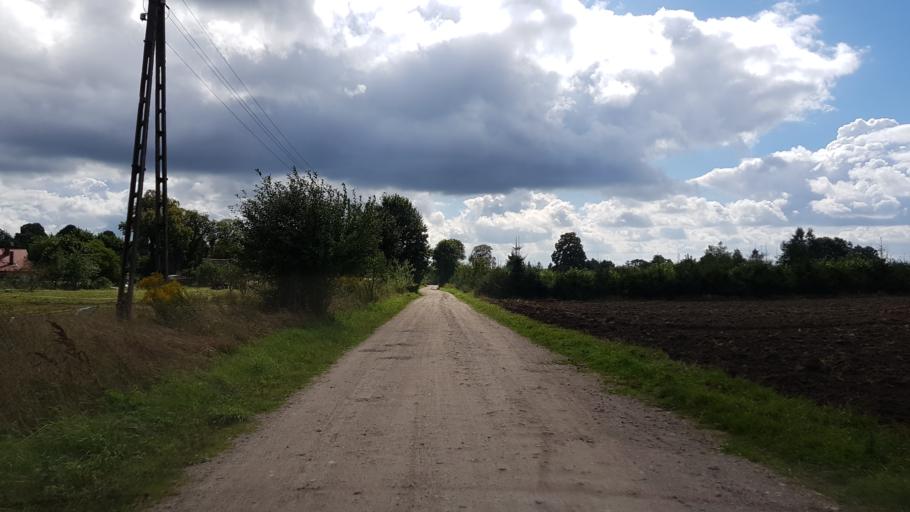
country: PL
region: West Pomeranian Voivodeship
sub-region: Powiat bialogardzki
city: Tychowo
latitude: 53.9958
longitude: 16.3054
